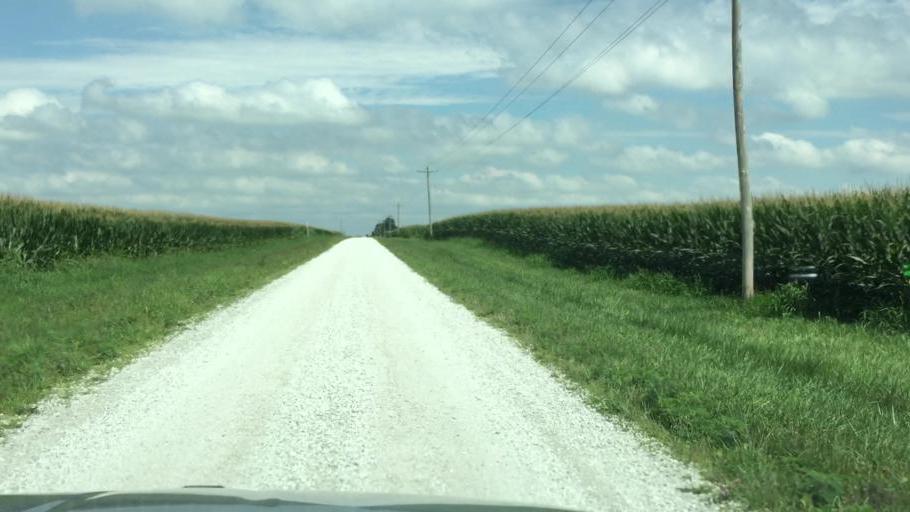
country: US
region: Illinois
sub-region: Hancock County
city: Nauvoo
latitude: 40.5218
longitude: -91.3035
